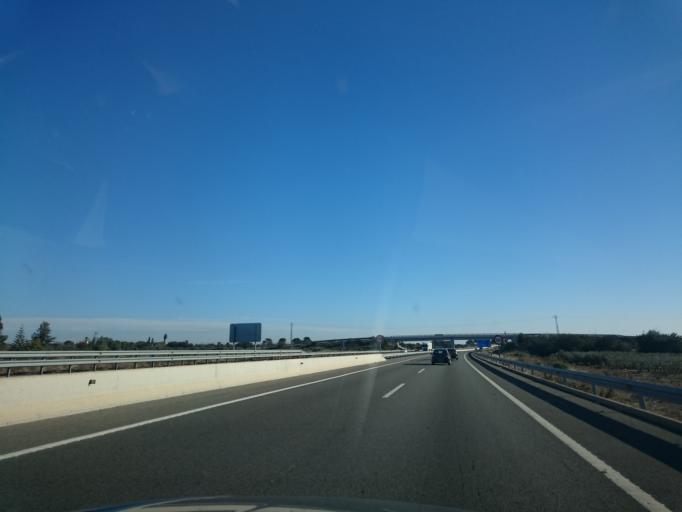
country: ES
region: Catalonia
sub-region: Provincia de Tarragona
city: Cambrils
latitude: 41.0852
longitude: 1.0453
